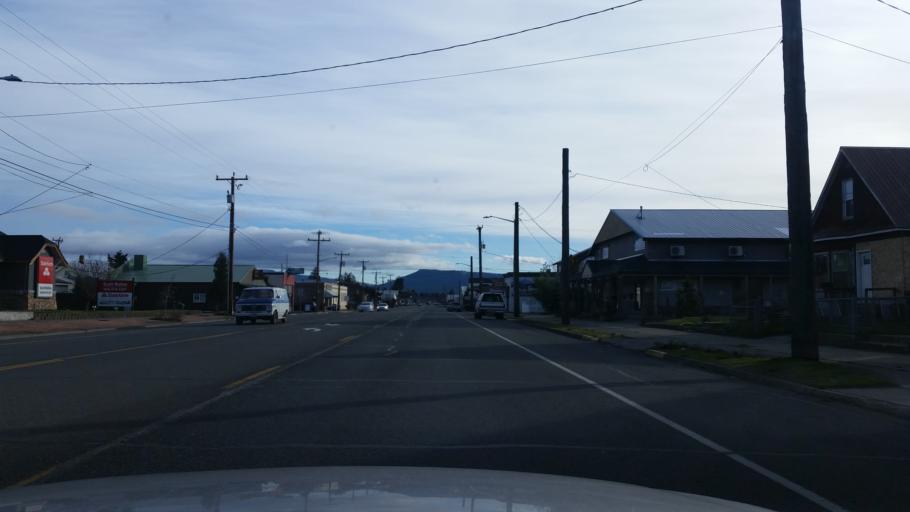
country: US
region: Washington
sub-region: Kittitas County
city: Cle Elum
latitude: 47.1942
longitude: -120.9329
